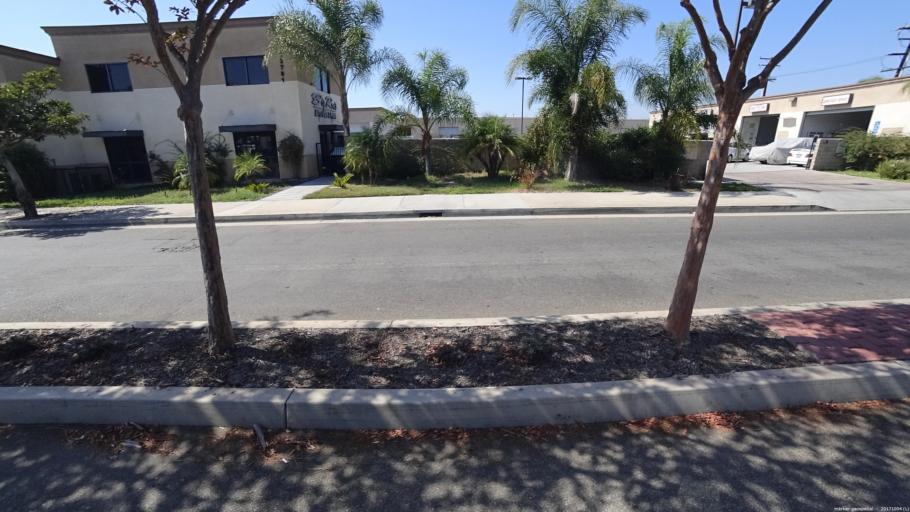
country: US
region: California
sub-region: Orange County
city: Garden Grove
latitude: 33.7773
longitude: -117.9453
